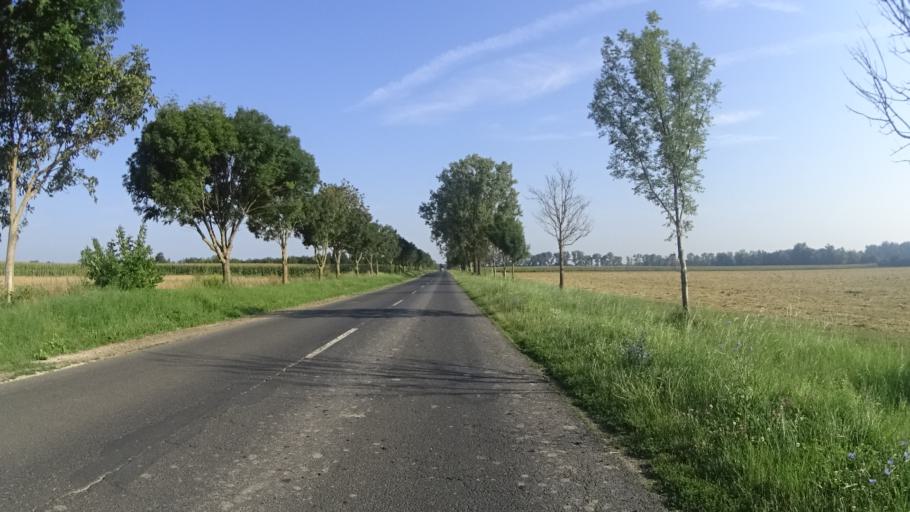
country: HU
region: Zala
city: Sarmellek
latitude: 46.6763
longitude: 17.1721
